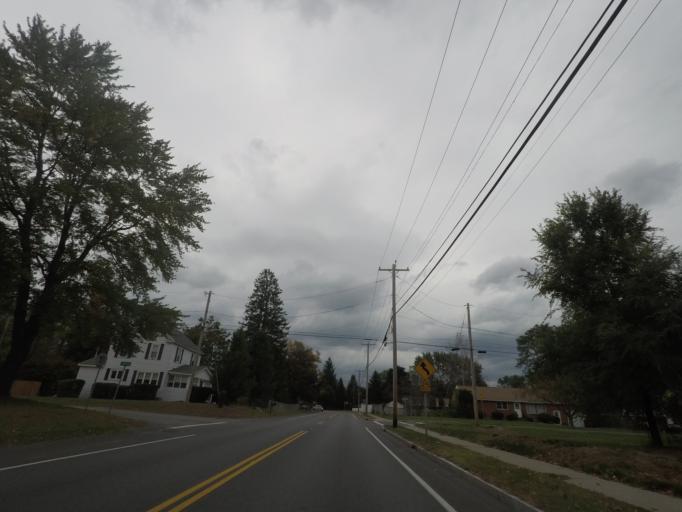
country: US
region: New York
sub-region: Albany County
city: McKownville
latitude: 42.6700
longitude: -73.8463
